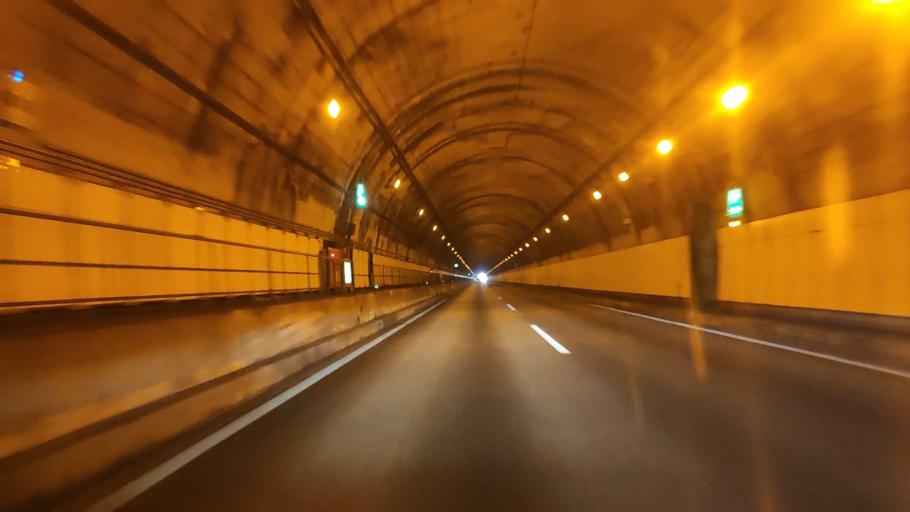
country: JP
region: Miyazaki
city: Miyakonojo
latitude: 31.8232
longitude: 131.2401
